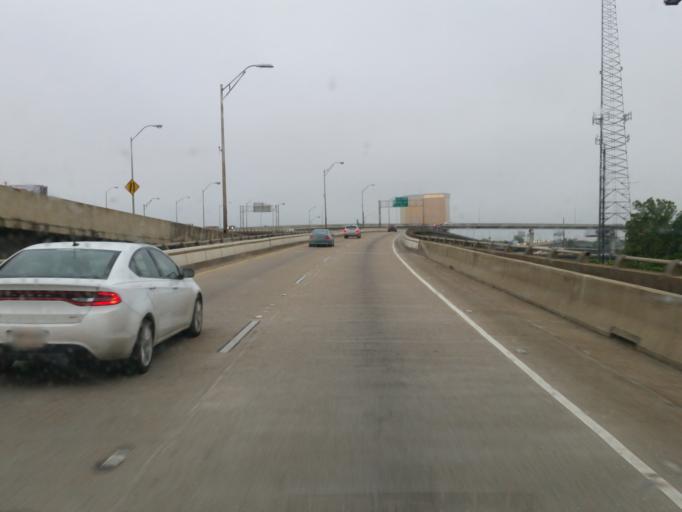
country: US
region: Louisiana
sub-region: Bossier Parish
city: Bossier City
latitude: 32.5080
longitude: -93.7447
